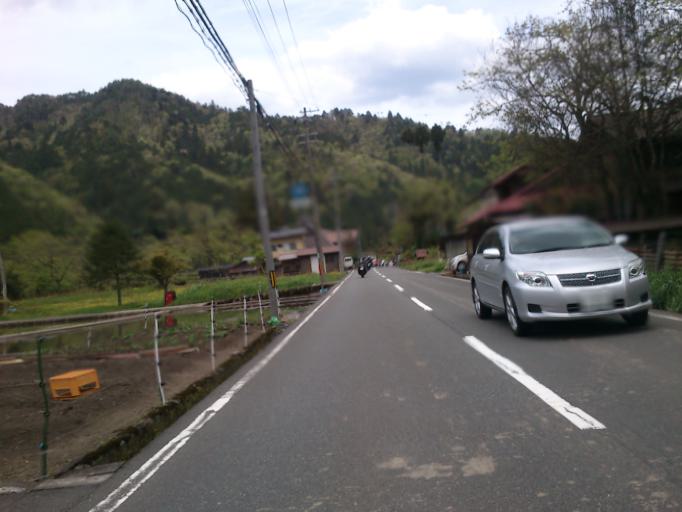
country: JP
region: Fukui
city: Obama
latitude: 35.2998
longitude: 135.6148
